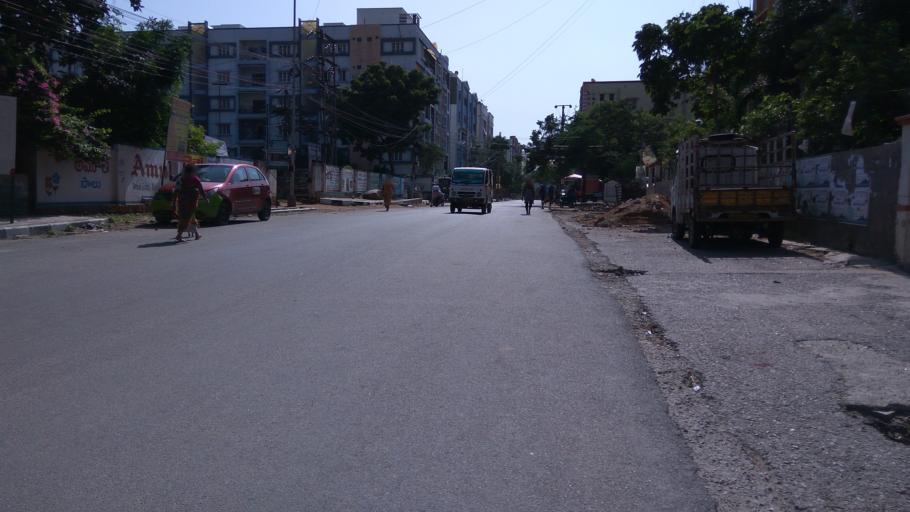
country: IN
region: Telangana
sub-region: Rangareddi
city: Kukatpalli
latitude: 17.4565
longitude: 78.4359
